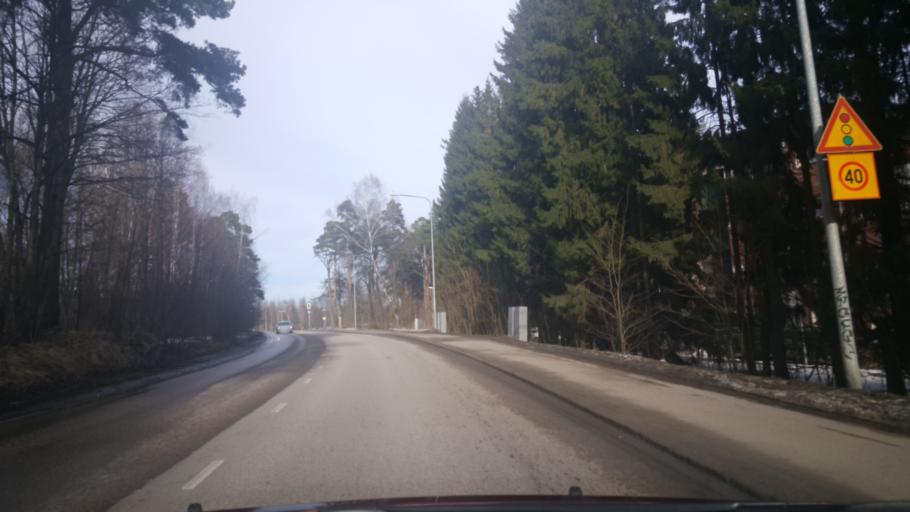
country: FI
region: Uusimaa
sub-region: Helsinki
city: Teekkarikylae
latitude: 60.2500
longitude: 24.8656
